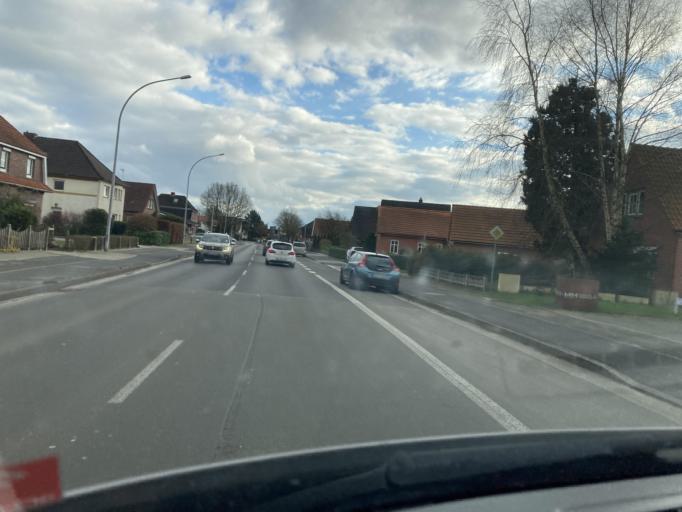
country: DE
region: Lower Saxony
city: Ostrhauderfehn
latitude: 53.1448
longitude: 7.5651
